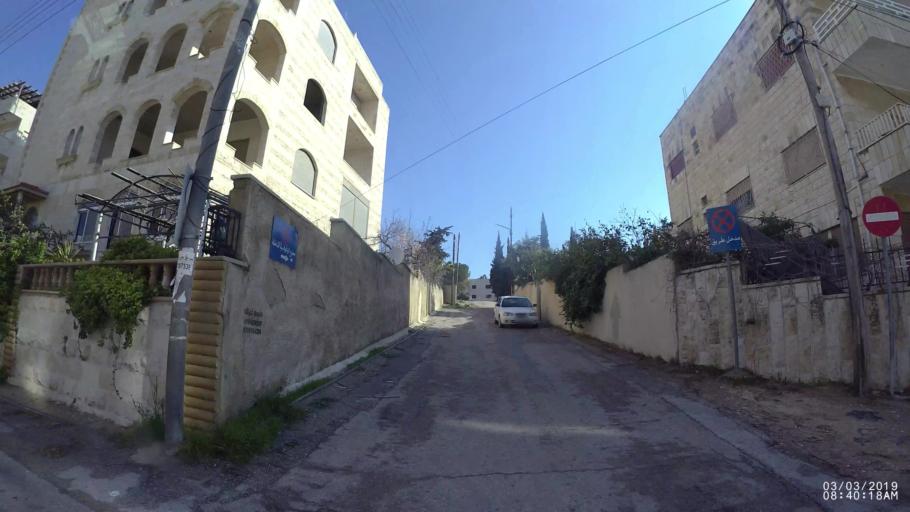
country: JO
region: Amman
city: Al Jubayhah
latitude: 31.9998
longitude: 35.8826
